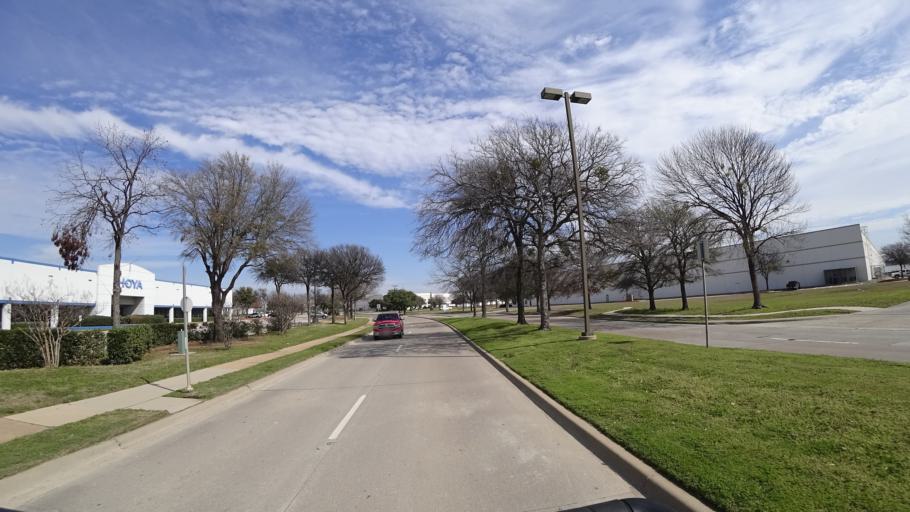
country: US
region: Texas
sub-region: Denton County
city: Lewisville
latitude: 33.0210
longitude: -96.9751
